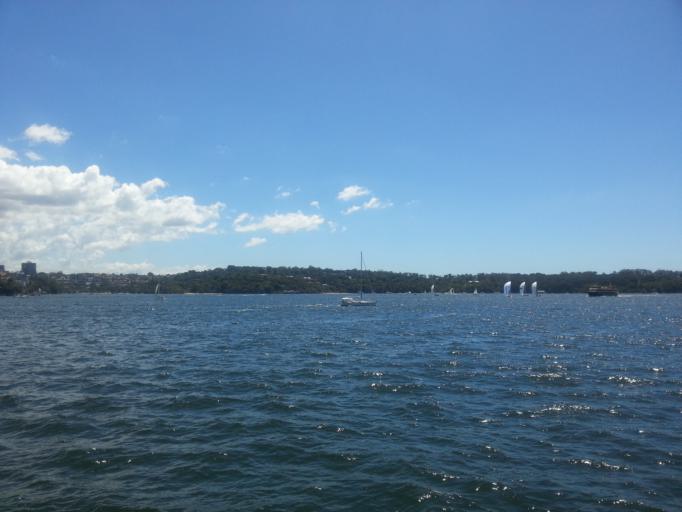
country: AU
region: New South Wales
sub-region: North Sydney
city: Kurraba Point
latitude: -33.8562
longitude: 151.2311
